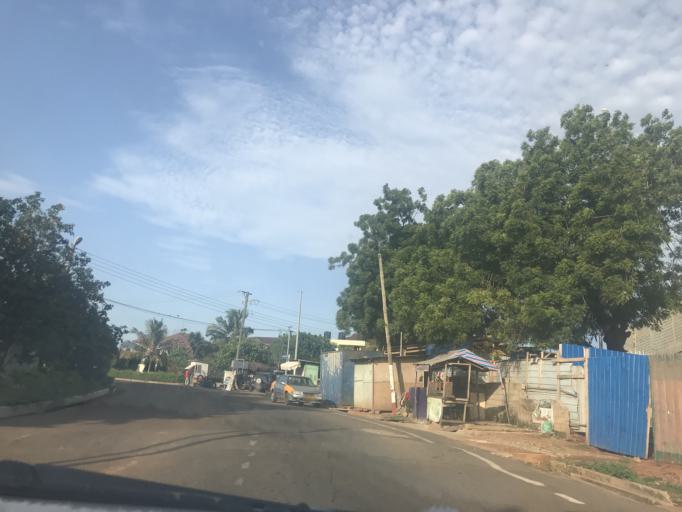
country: GH
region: Greater Accra
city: Medina Estates
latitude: 5.6688
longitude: -0.1782
